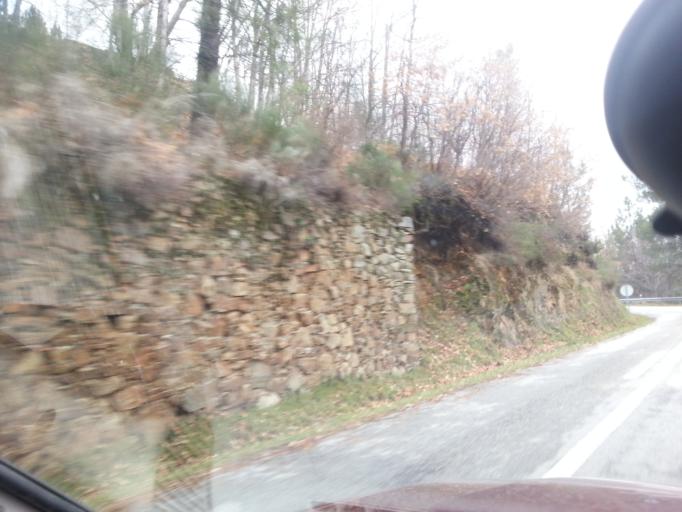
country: PT
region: Guarda
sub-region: Manteigas
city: Manteigas
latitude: 40.4117
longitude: -7.5258
